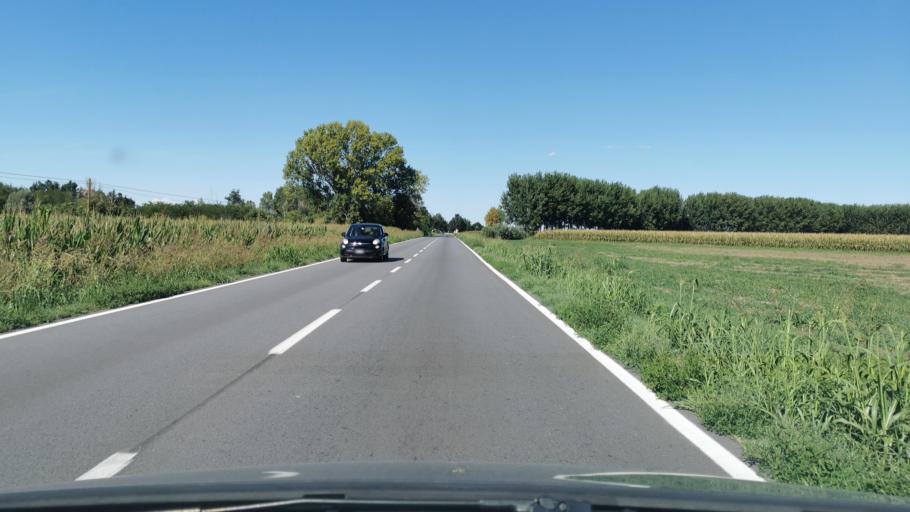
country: IT
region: Piedmont
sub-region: Provincia di Cuneo
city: Genola
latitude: 44.5736
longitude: 7.6345
